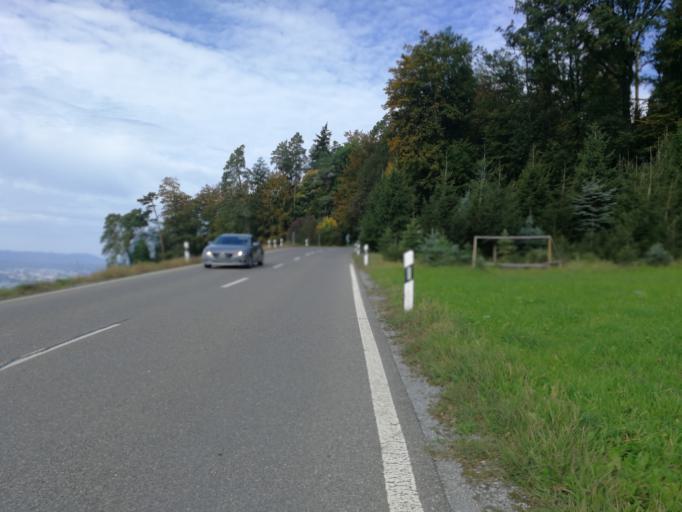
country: CH
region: Zurich
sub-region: Bezirk Meilen
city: Oetwil am See
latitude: 47.2626
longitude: 8.7106
